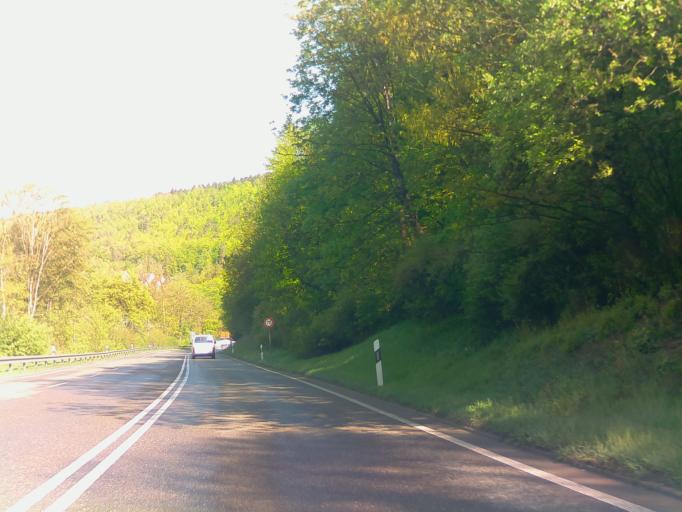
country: DE
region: Baden-Wuerttemberg
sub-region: Karlsruhe Region
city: Nagold
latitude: 48.5477
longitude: 8.7459
